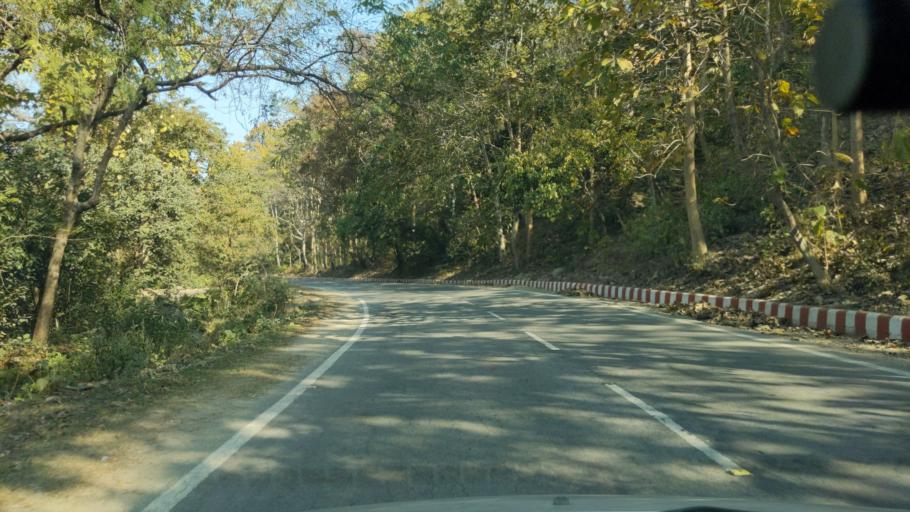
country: IN
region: Uttarakhand
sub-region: Naini Tal
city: Ramnagar
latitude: 29.3929
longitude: 79.1380
